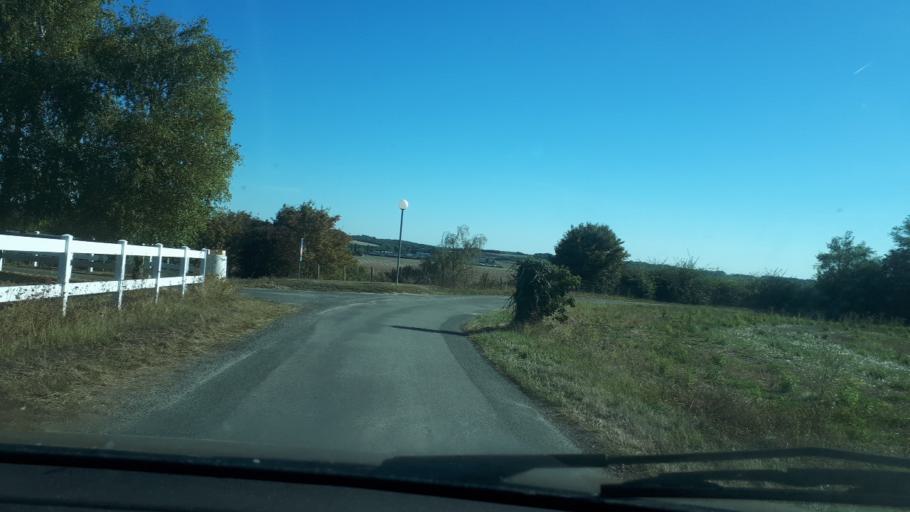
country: FR
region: Centre
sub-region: Departement du Loir-et-Cher
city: Naveil
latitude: 47.7966
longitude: 1.0191
